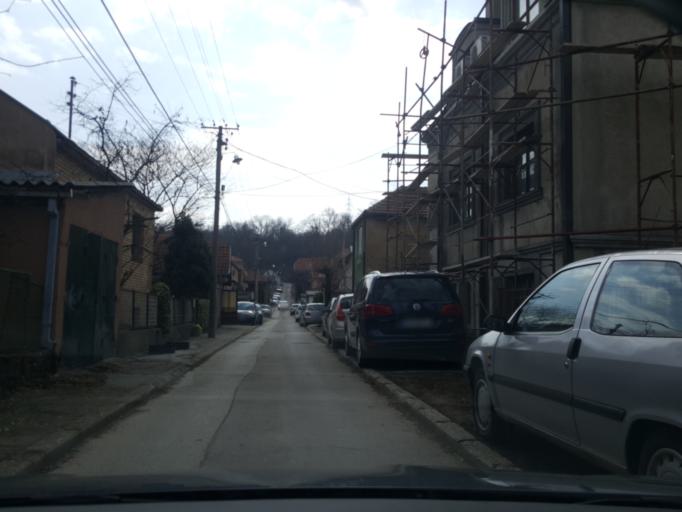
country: RS
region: Central Serbia
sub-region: Nisavski Okrug
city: Nis
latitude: 43.3138
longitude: 21.8659
